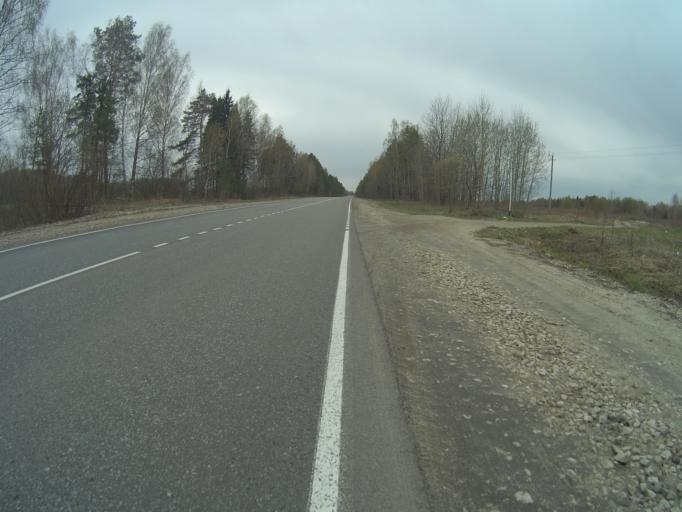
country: RU
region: Vladimir
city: Golovino
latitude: 55.9966
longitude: 40.5623
